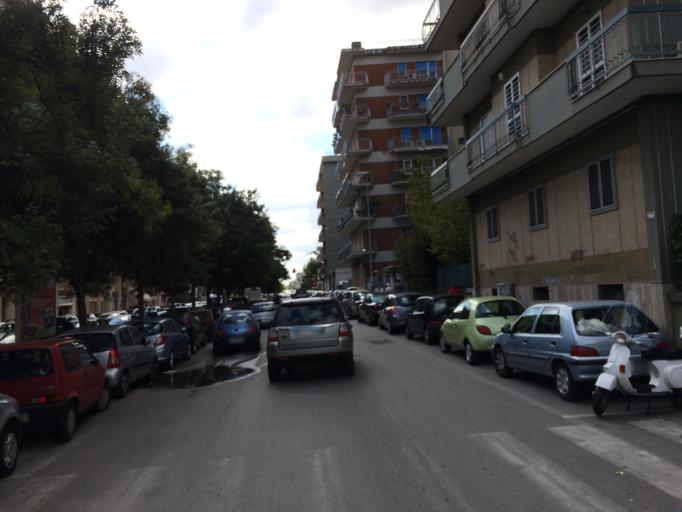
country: IT
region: Apulia
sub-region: Provincia di Bari
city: Bari
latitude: 41.1036
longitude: 16.8824
